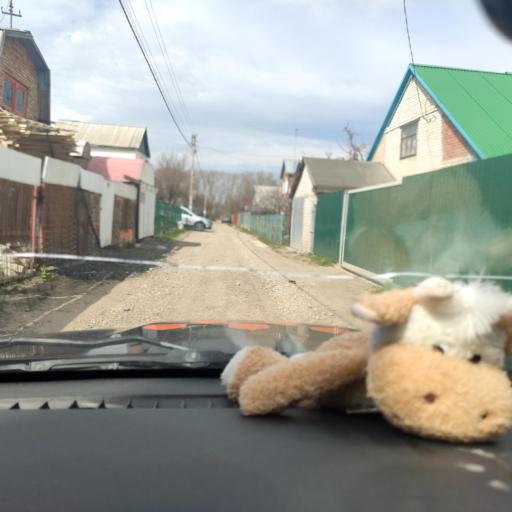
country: RU
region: Samara
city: Tol'yatti
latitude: 53.6030
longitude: 49.2413
